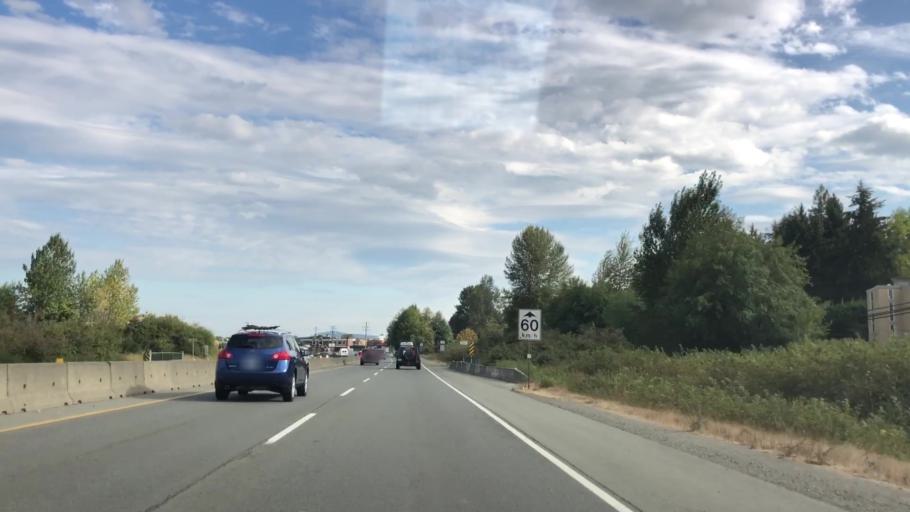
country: CA
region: British Columbia
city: Duncan
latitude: 48.7909
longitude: -123.7119
